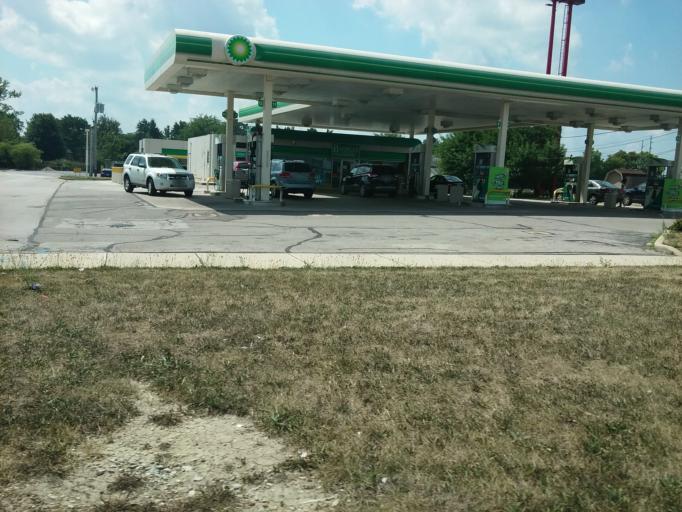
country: US
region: Ohio
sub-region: Wood County
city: Bowling Green
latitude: 41.3744
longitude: -83.6196
